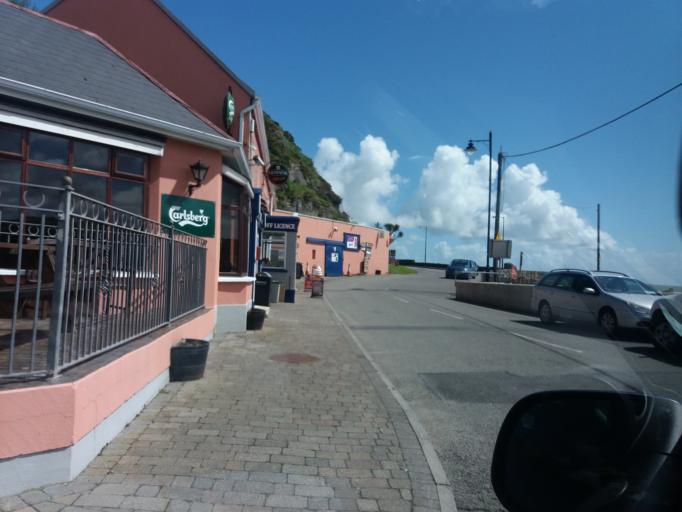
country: IE
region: Munster
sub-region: Waterford
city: Dunmore East
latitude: 52.2450
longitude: -6.9684
